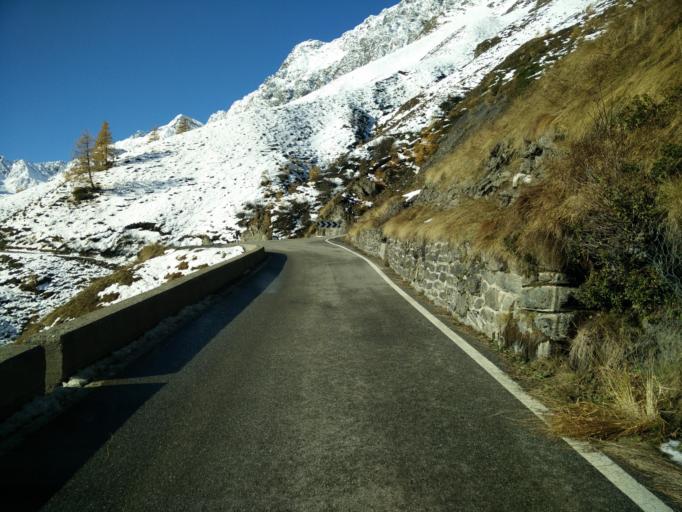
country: IT
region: Trentino-Alto Adige
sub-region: Bolzano
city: Moso in Passiria
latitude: 46.8822
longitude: 11.1127
